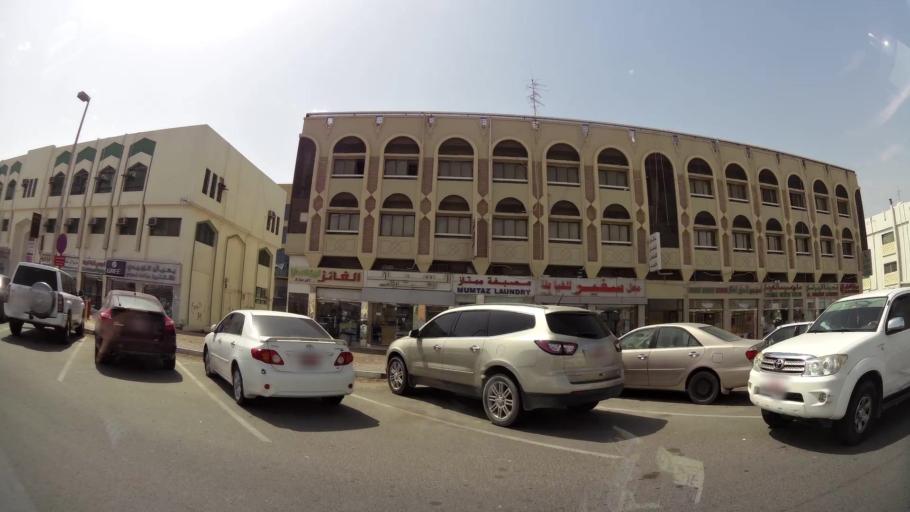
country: AE
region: Abu Dhabi
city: Abu Dhabi
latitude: 24.2967
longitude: 54.6392
